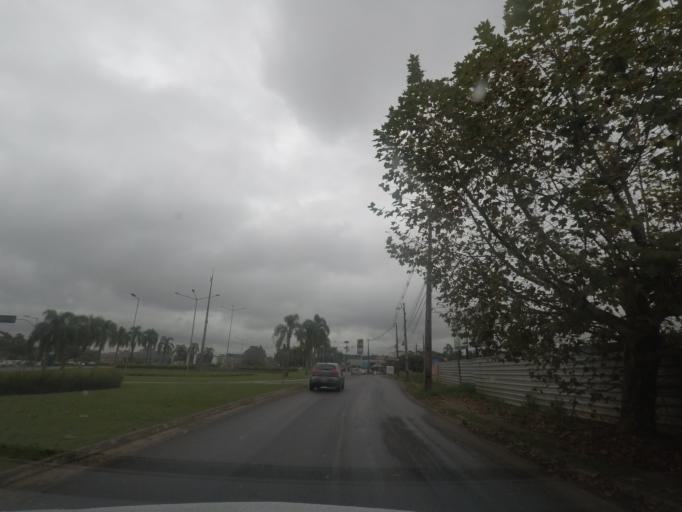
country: BR
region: Parana
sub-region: Pinhais
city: Pinhais
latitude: -25.3919
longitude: -49.1625
